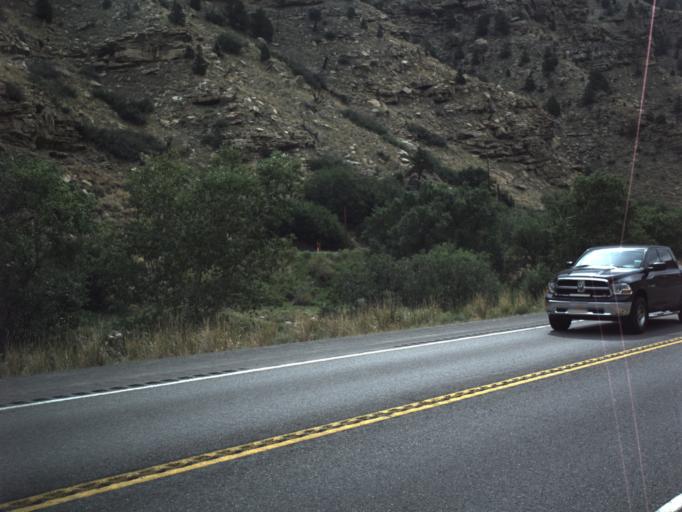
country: US
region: Utah
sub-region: Carbon County
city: Helper
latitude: 39.7579
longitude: -110.8901
